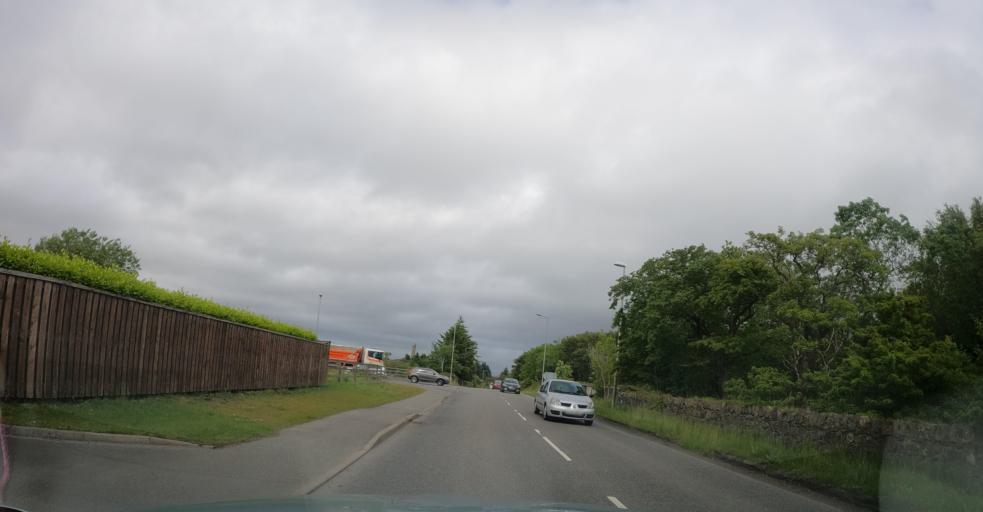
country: GB
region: Scotland
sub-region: Eilean Siar
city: Isle of Lewis
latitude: 58.2176
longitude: -6.4075
